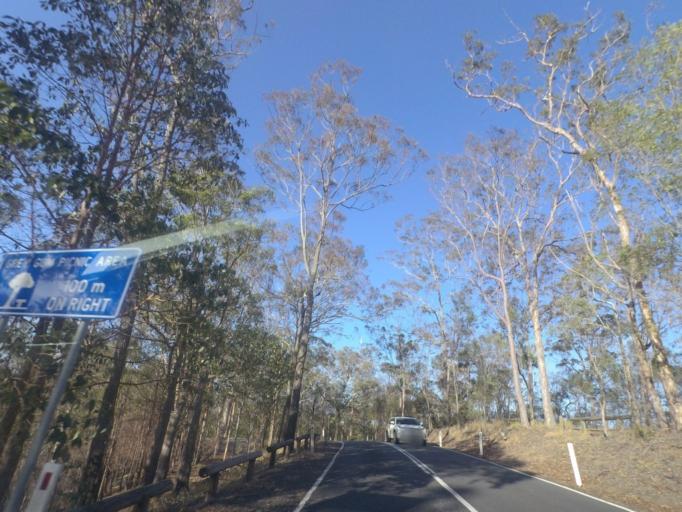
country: AU
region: Queensland
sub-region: Brisbane
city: Kenmore Hills
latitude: -27.4690
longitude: 152.9425
